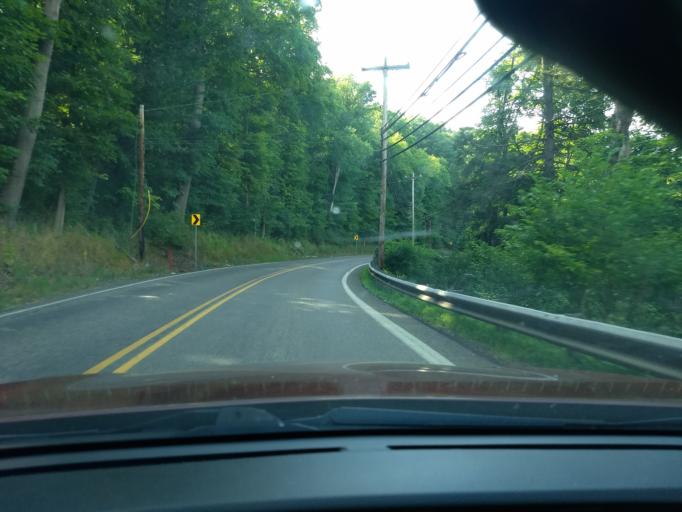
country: US
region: Pennsylvania
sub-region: Allegheny County
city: Bell Acres
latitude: 40.5989
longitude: -80.1882
